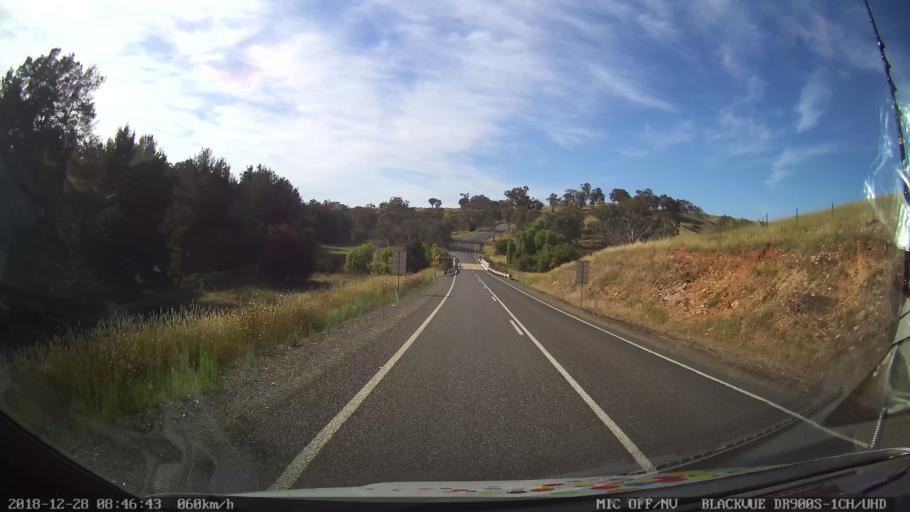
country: AU
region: New South Wales
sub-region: Upper Lachlan Shire
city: Crookwell
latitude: -34.0215
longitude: 149.3322
